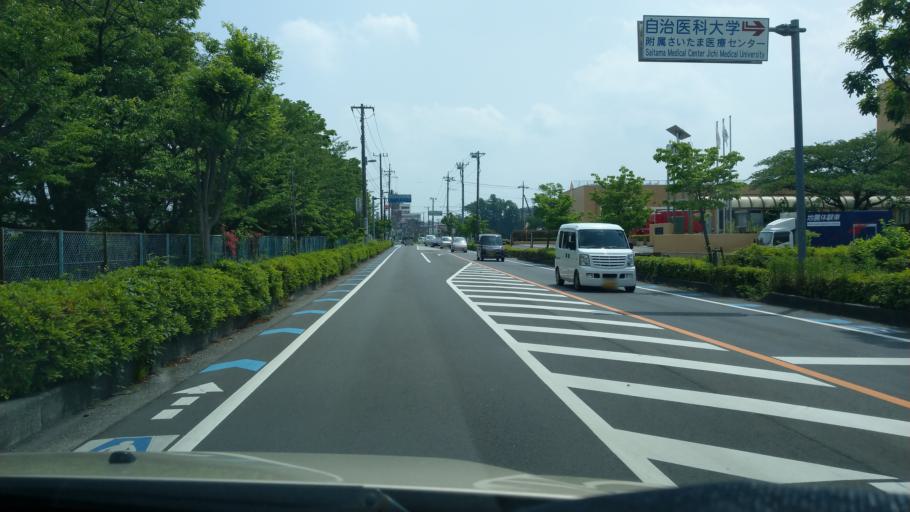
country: JP
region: Saitama
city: Saitama
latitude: 35.9080
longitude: 139.6467
